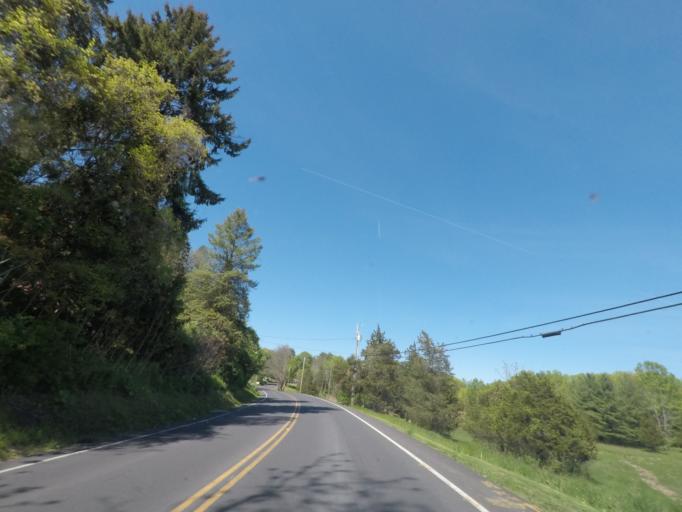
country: US
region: New York
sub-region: Ulster County
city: Lake Katrine
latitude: 42.0045
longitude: -73.9667
